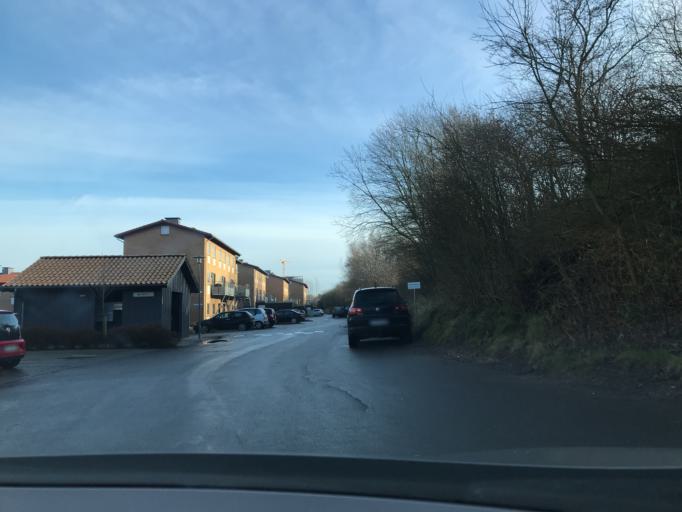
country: DK
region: South Denmark
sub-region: Sonderborg Kommune
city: Dybbol
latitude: 54.9150
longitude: 9.7688
